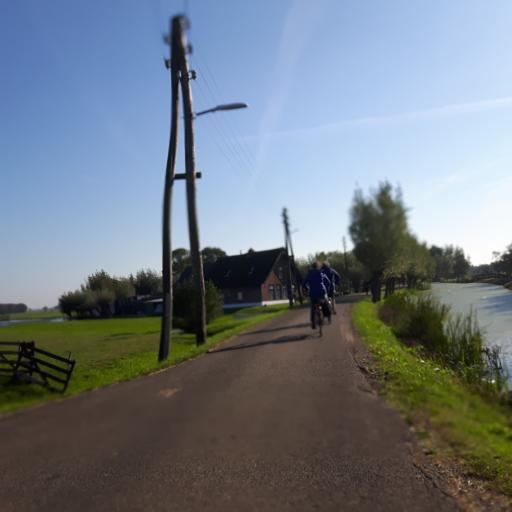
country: NL
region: South Holland
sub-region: Gemeente Vlist
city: Vlist
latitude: 51.9689
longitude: 4.8333
